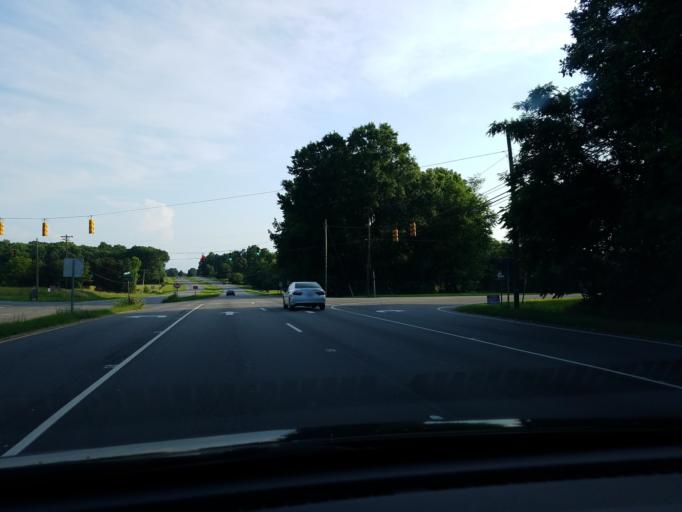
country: US
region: North Carolina
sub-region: Durham County
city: Gorman
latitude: 36.1178
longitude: -78.9031
